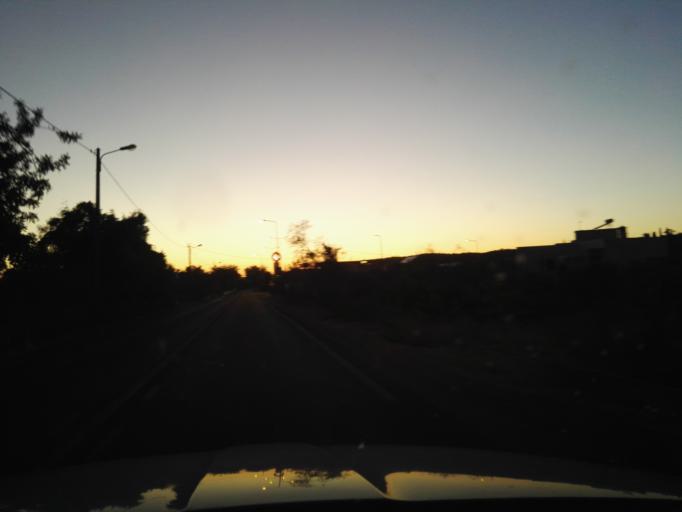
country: PT
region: Faro
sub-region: Sao Bras de Alportel
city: Sao Bras de Alportel
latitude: 37.1507
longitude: -7.9387
